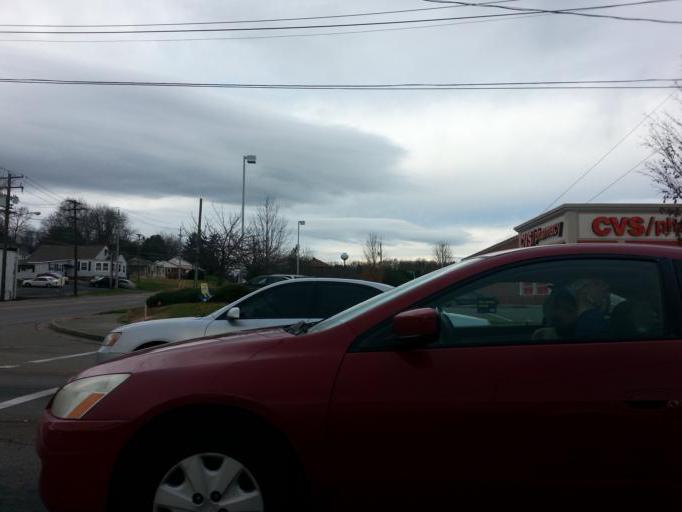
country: US
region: Tennessee
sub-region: Washington County
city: Johnson City
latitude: 36.3151
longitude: -82.3740
